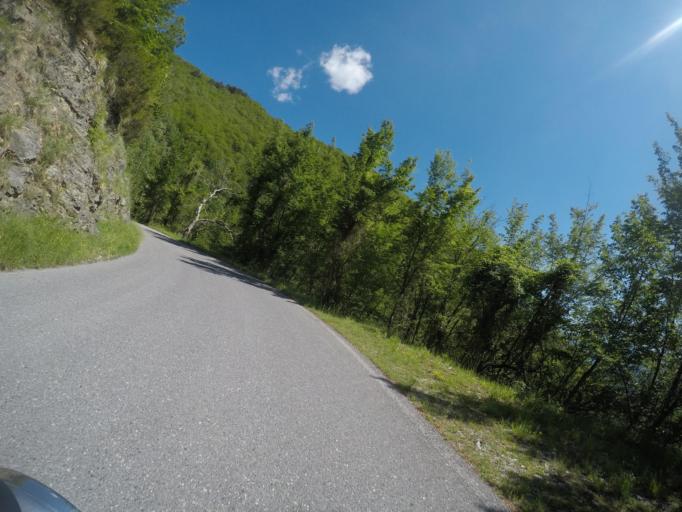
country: IT
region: Tuscany
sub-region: Provincia di Lucca
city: Careggine
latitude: 44.0740
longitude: 10.3309
